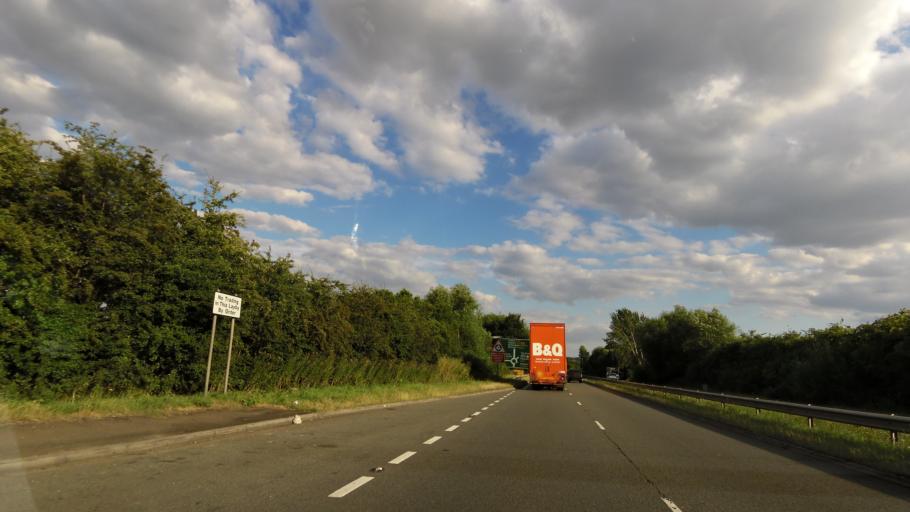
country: GB
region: England
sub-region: Nottinghamshire
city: Worksop
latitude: 53.3059
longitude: -1.1388
